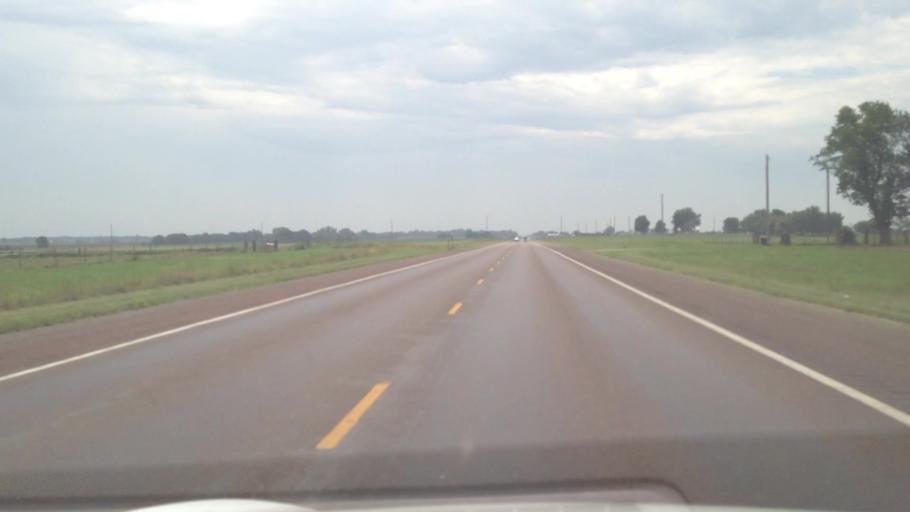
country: US
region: Kansas
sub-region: Crawford County
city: Girard
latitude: 37.4633
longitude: -94.8331
